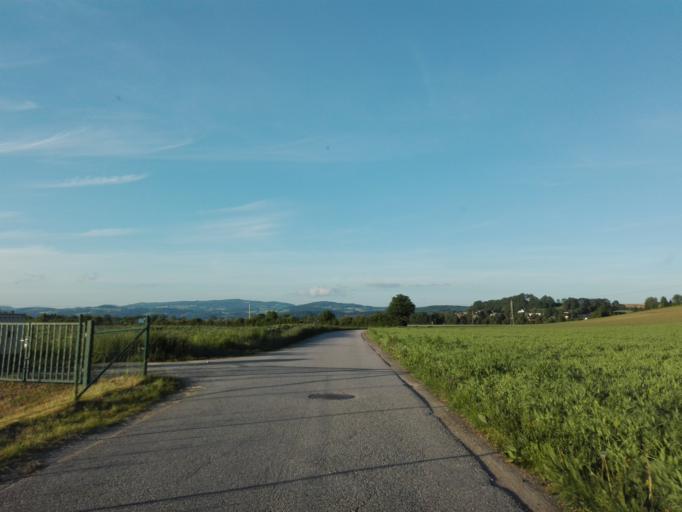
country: AT
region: Upper Austria
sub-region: Politischer Bezirk Urfahr-Umgebung
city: Goldworth
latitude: 48.2816
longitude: 14.1318
